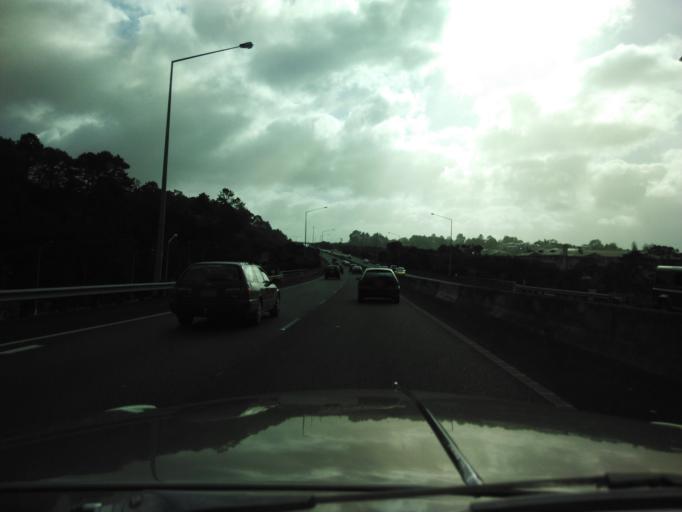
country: NZ
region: Auckland
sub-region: Auckland
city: Rothesay Bay
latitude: -36.7192
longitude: 174.7129
